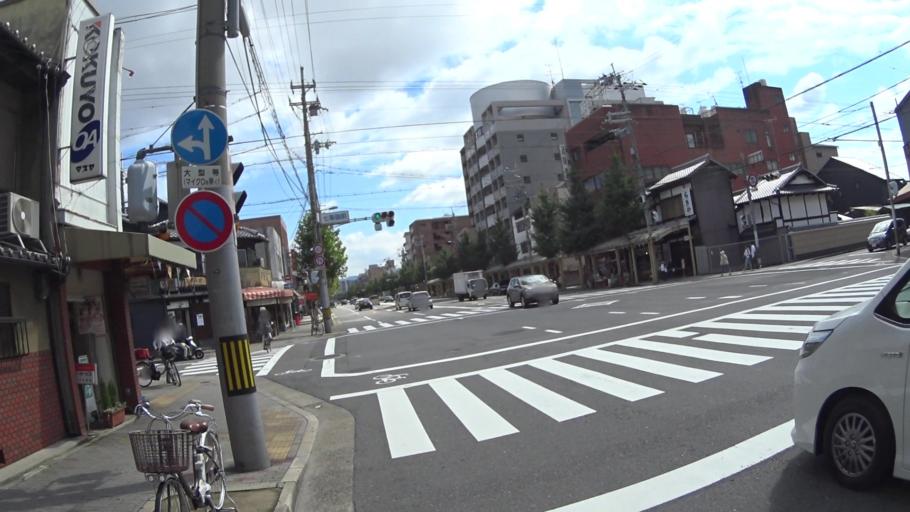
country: JP
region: Kyoto
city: Kyoto
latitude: 34.9893
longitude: 135.7361
